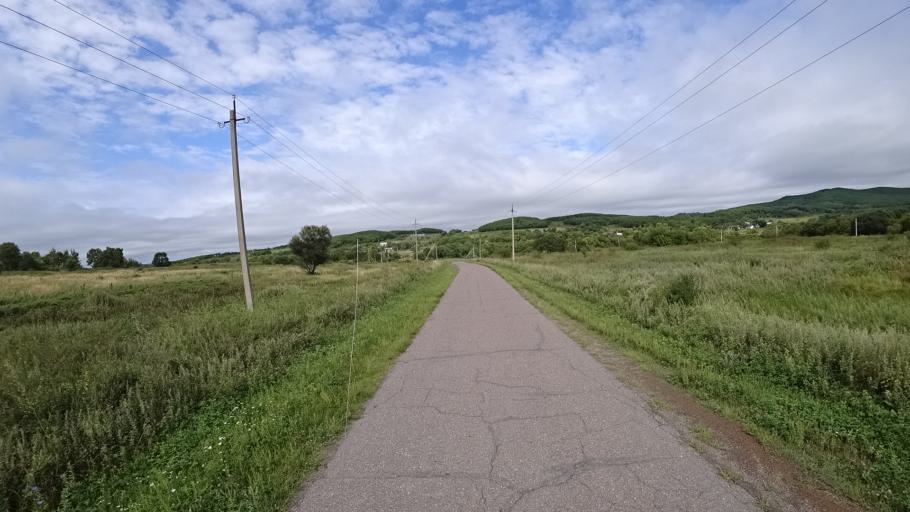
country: RU
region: Primorskiy
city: Lyalichi
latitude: 44.1330
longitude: 132.3878
